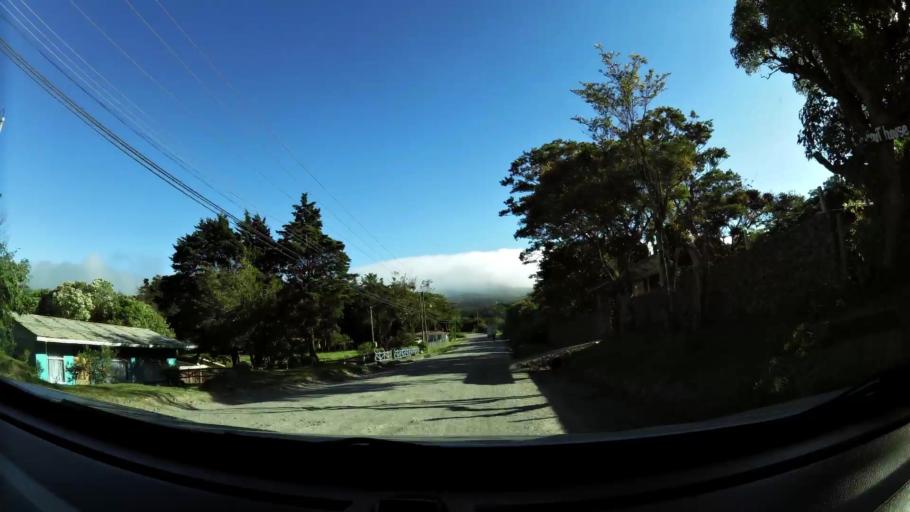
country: CR
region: Guanacaste
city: Juntas
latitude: 10.3060
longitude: -84.8318
